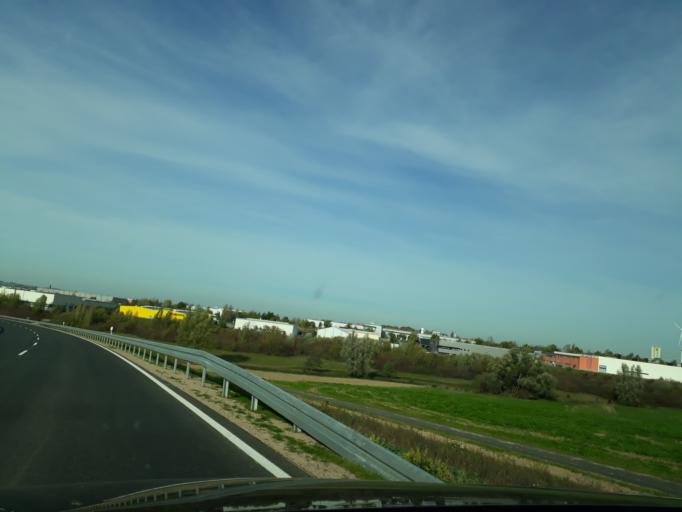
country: DE
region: Saxony
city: Mochau
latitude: 51.1166
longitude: 13.1665
